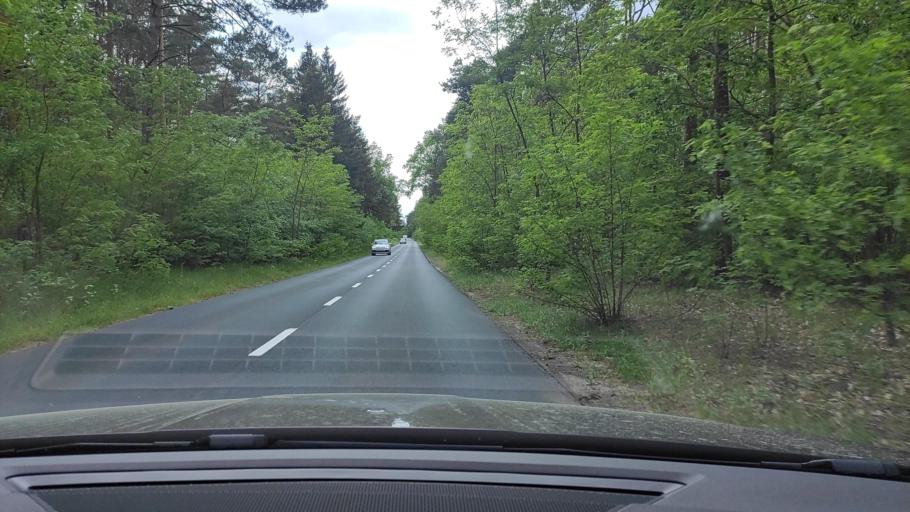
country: PL
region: Greater Poland Voivodeship
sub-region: Powiat poznanski
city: Swarzedz
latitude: 52.3884
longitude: 17.0434
